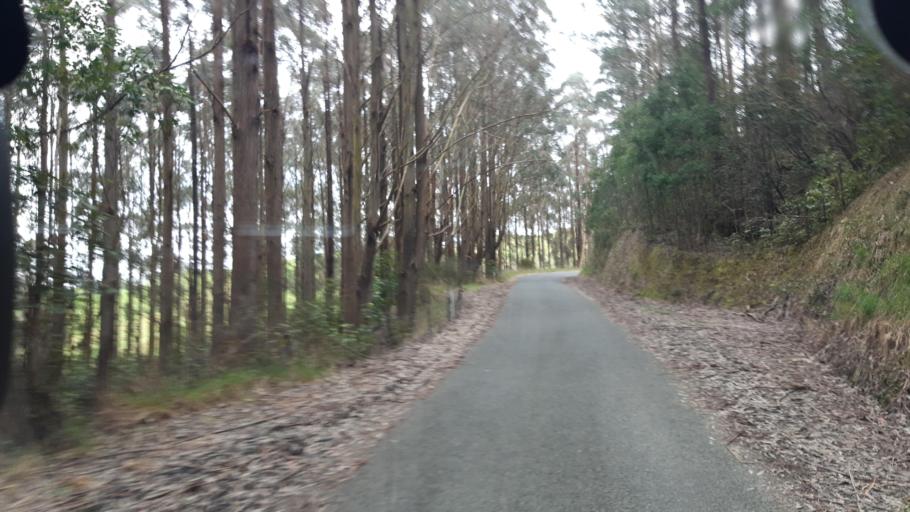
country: NZ
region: Tasman
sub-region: Tasman District
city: Motueka
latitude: -41.2665
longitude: 172.8888
